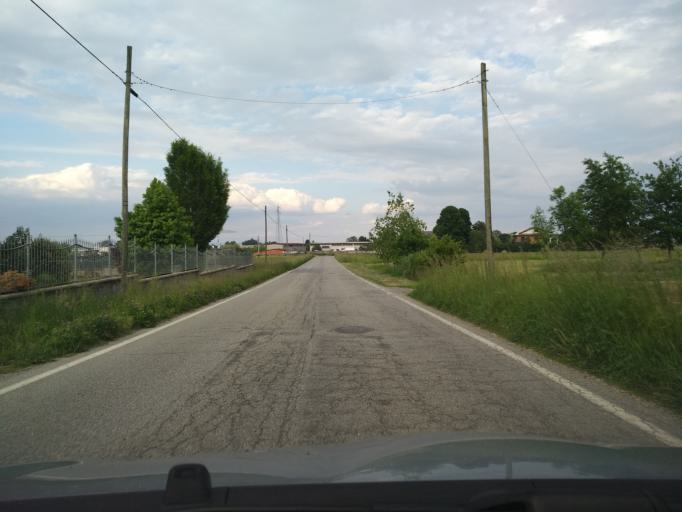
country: IT
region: Piedmont
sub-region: Provincia di Torino
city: Frossasco
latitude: 44.9066
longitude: 7.3527
